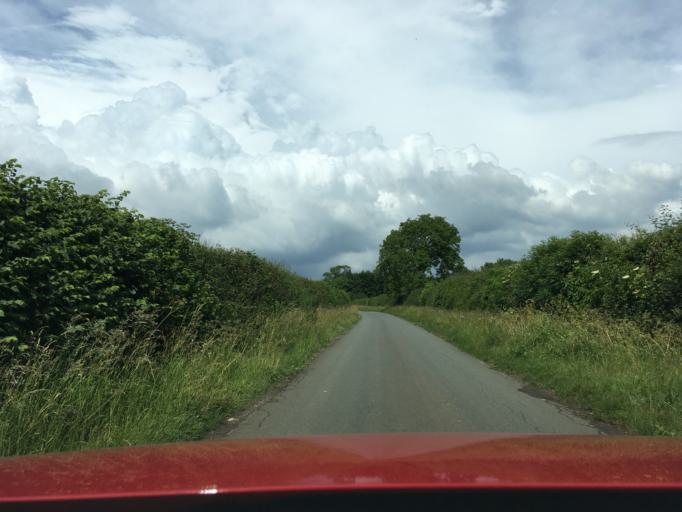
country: GB
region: England
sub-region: Gloucestershire
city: Chalford
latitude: 51.6903
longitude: -2.1290
